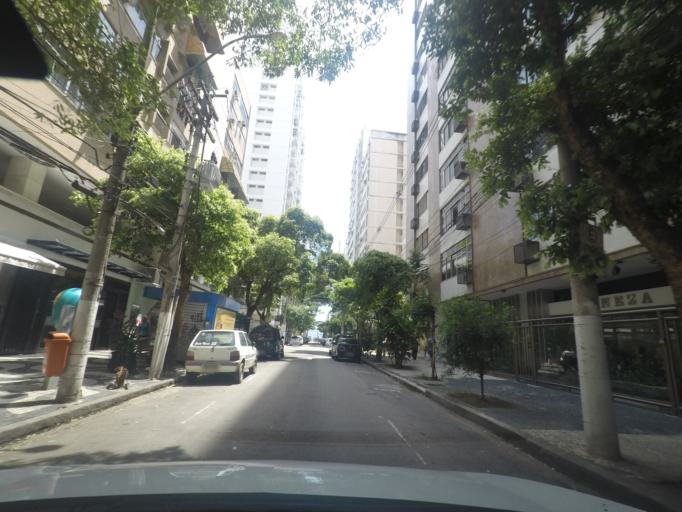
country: BR
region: Rio de Janeiro
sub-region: Niteroi
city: Niteroi
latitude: -22.9068
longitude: -43.1098
